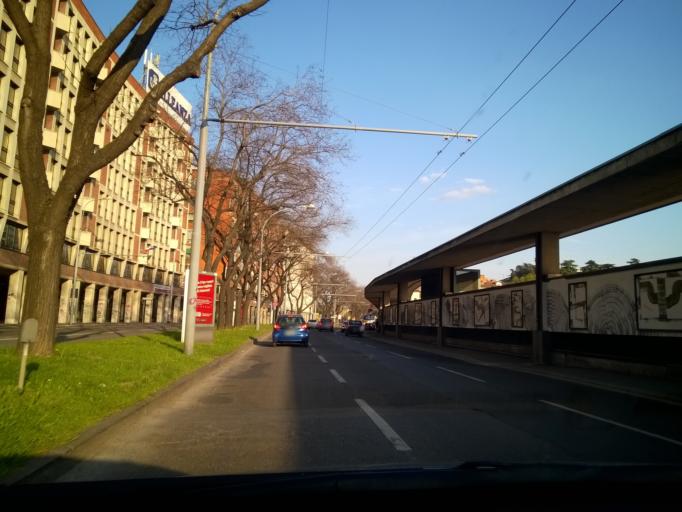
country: IT
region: Emilia-Romagna
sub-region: Provincia di Bologna
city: Bologna
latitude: 44.5042
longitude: 11.3478
